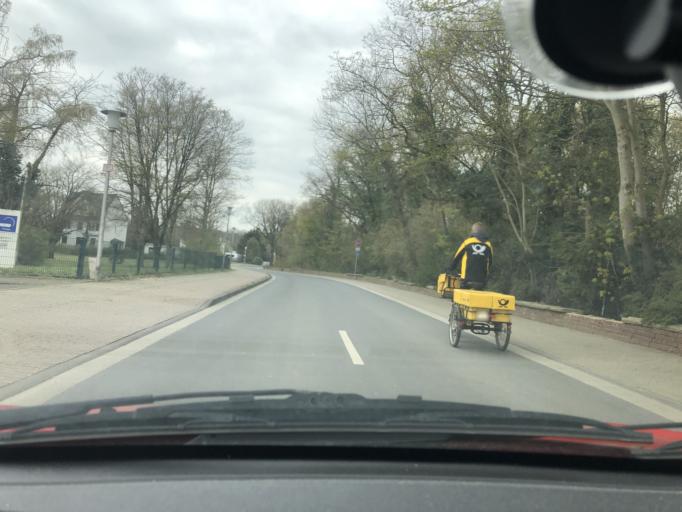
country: DE
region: North Rhine-Westphalia
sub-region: Regierungsbezirk Dusseldorf
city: Kamp-Lintfort
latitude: 51.4923
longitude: 6.5445
